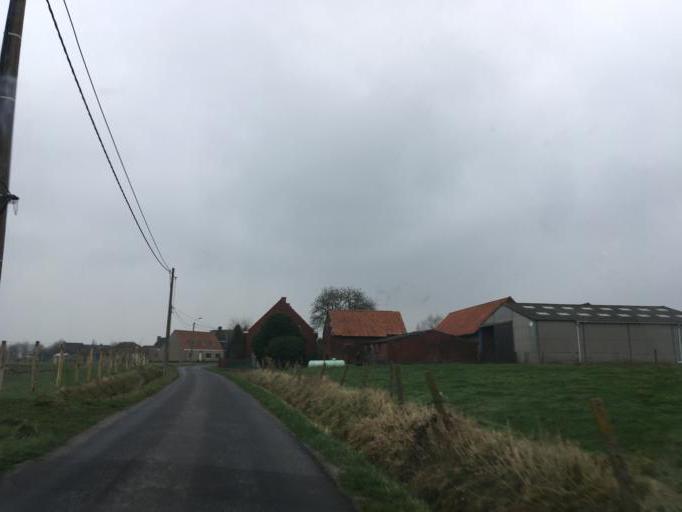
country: BE
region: Flanders
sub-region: Provincie West-Vlaanderen
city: Roeselare
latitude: 50.9780
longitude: 3.1395
